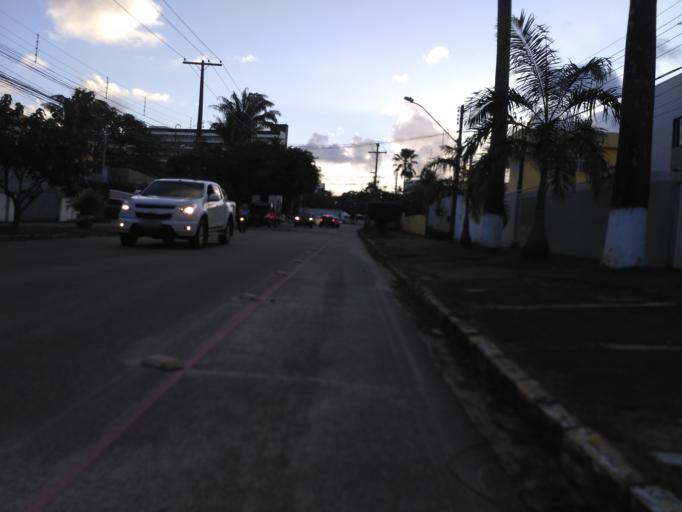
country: BR
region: Pernambuco
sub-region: Recife
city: Recife
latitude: -8.0462
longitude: -34.9431
